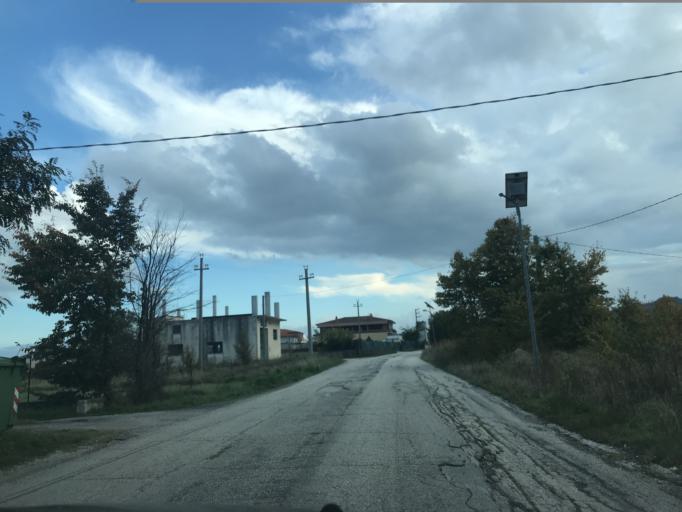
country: IT
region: Molise
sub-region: Provincia di Isernia
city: Bagnoli del Trigno
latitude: 41.6959
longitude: 14.4613
